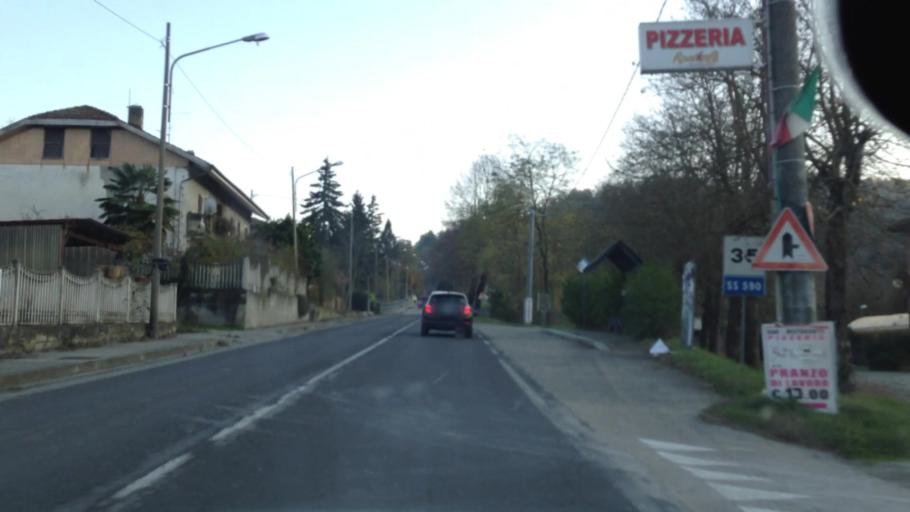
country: IT
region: Piedmont
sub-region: Provincia di Torino
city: Brozolo
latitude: 45.1219
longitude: 8.0590
